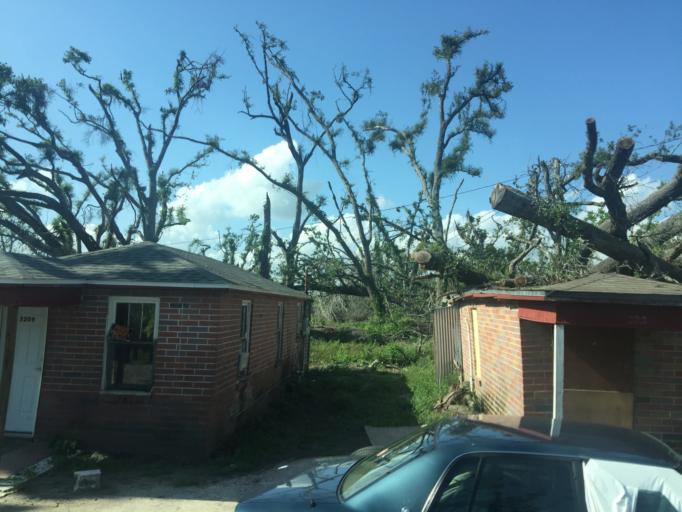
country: US
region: Florida
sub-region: Bay County
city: Springfield
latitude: 30.1466
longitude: -85.6187
